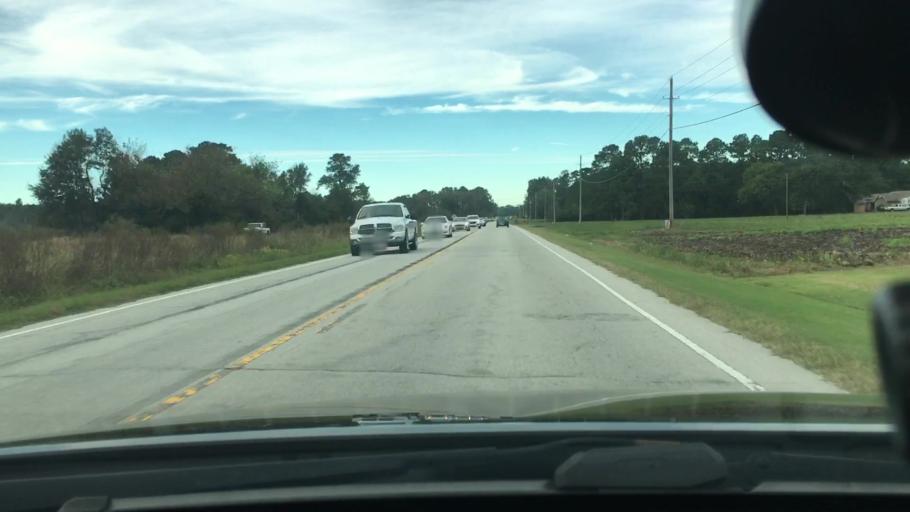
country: US
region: North Carolina
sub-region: Pitt County
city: Windsor
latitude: 35.5186
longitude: -77.3192
